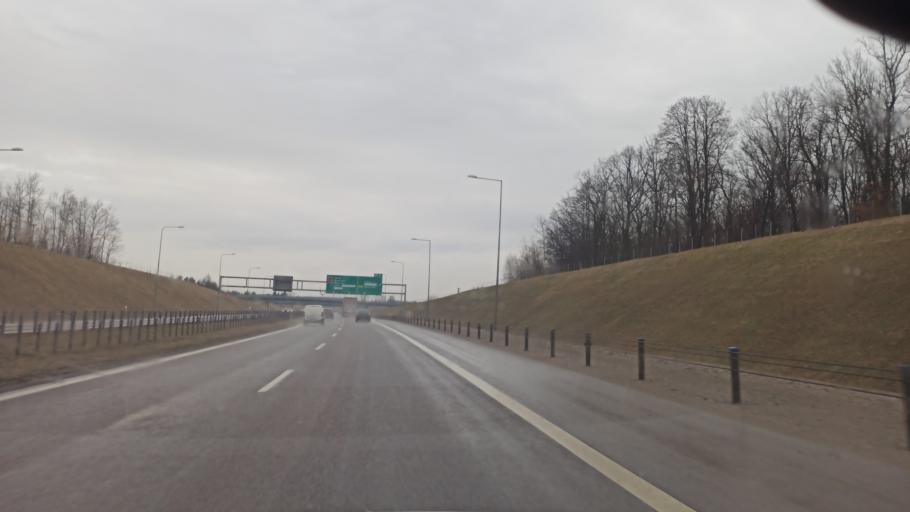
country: PL
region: Lublin Voivodeship
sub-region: Powiat lubelski
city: Kozubszczyzna
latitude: 51.2065
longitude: 22.4446
